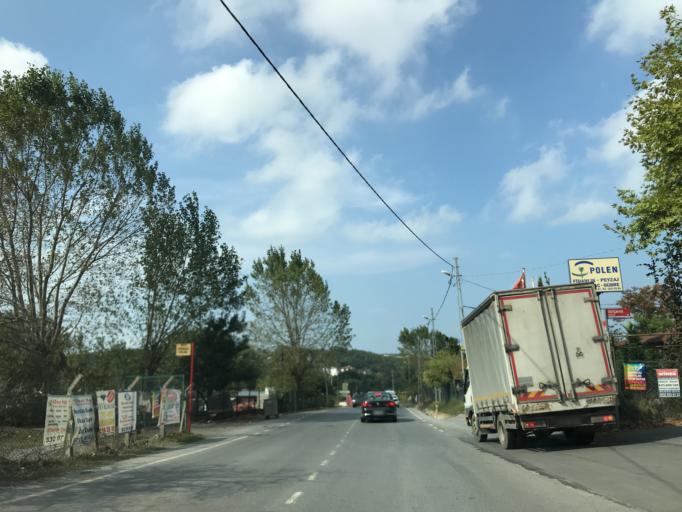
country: TR
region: Istanbul
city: Arikoey
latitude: 41.2170
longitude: 29.0352
